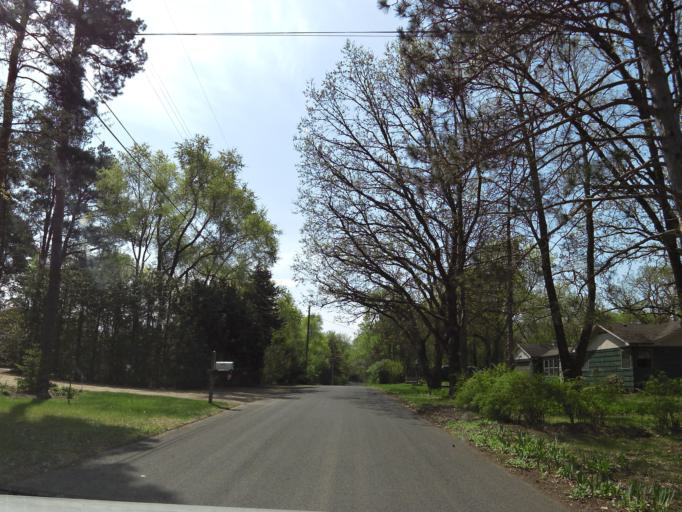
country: US
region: Minnesota
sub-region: Washington County
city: Lake Saint Croix Beach
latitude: 44.9183
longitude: -92.7697
